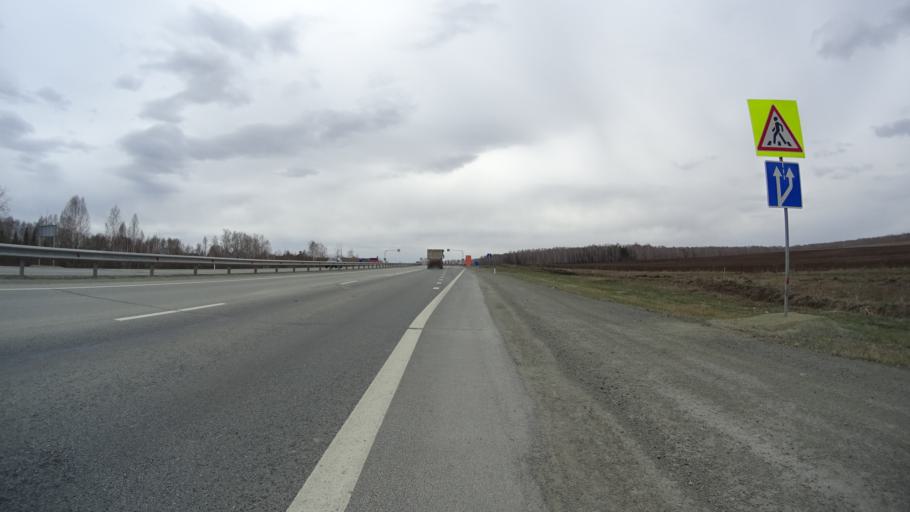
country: RU
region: Chelyabinsk
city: Yemanzhelinka
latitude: 54.8253
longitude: 61.3099
